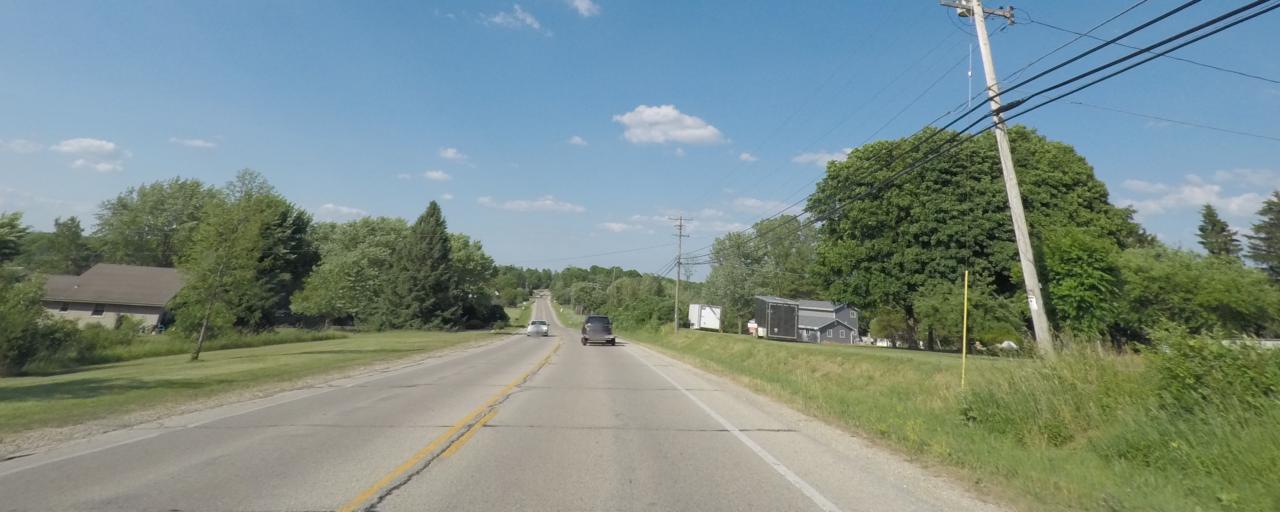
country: US
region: Wisconsin
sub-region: Waukesha County
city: Big Bend
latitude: 42.8731
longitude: -88.2149
